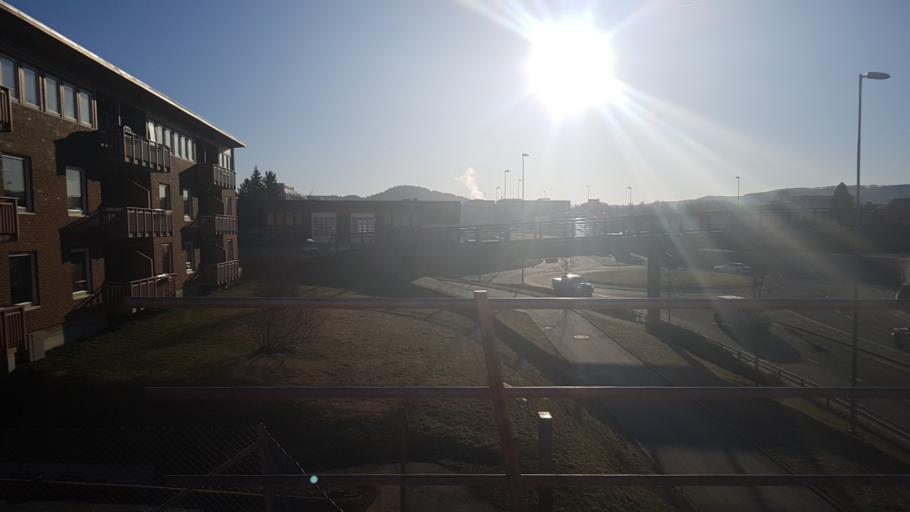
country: NO
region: Nord-Trondelag
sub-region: Stjordal
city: Stjordal
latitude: 63.4663
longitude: 10.9138
